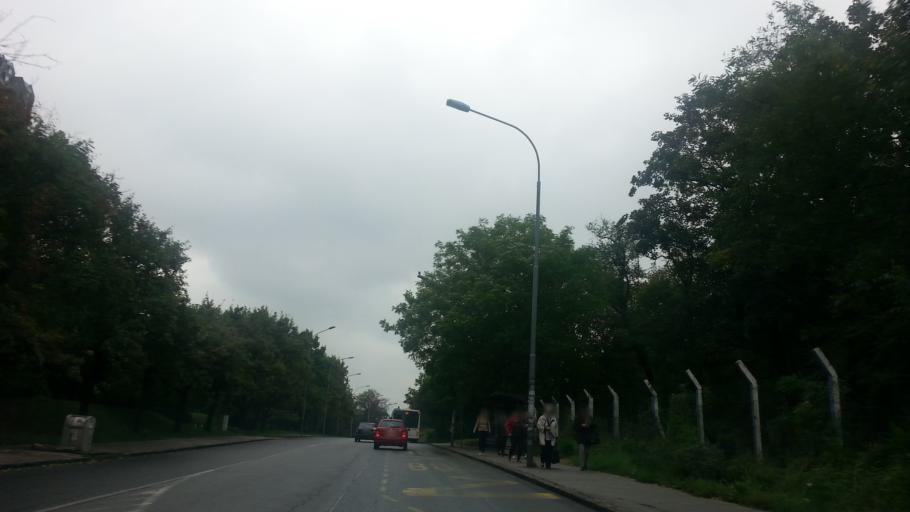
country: RS
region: Central Serbia
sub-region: Belgrade
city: Vozdovac
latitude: 44.7596
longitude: 20.4730
